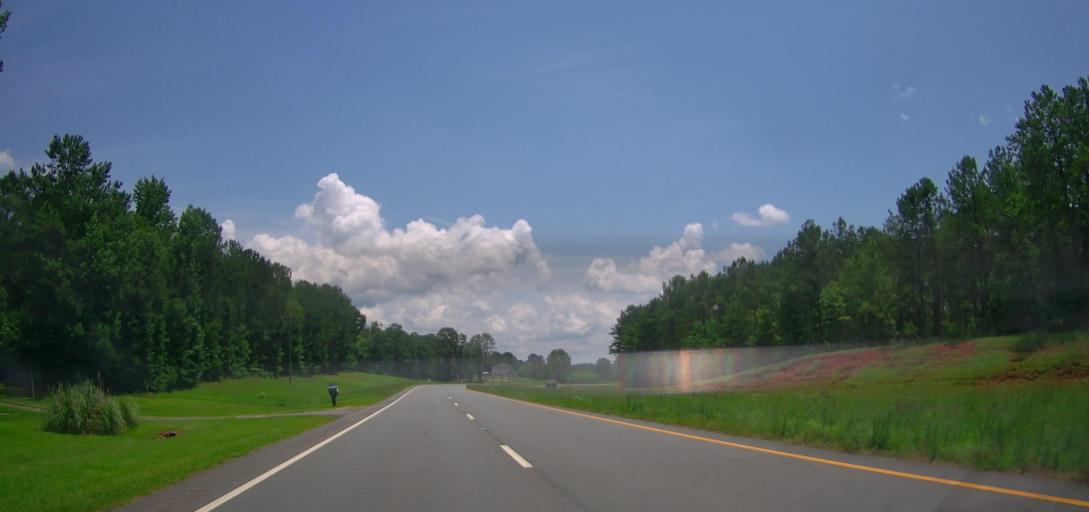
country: US
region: Georgia
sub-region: Upson County
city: Thomaston
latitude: 32.8076
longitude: -84.2803
